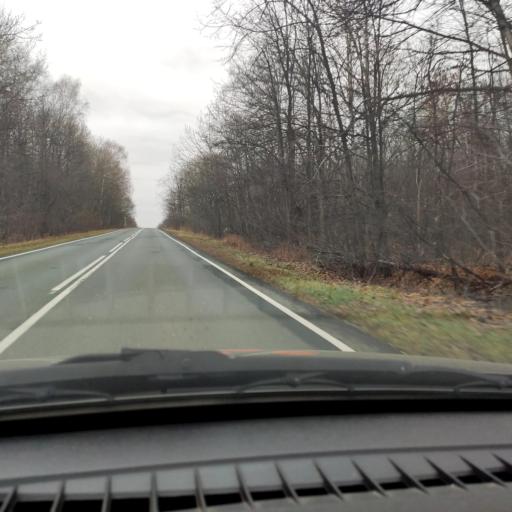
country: RU
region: Samara
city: Zhigulevsk
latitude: 53.3438
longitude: 49.5459
